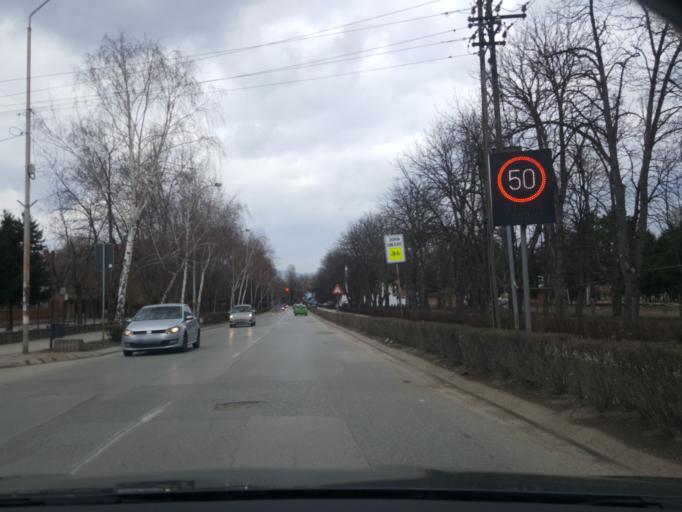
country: RS
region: Central Serbia
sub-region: Nisavski Okrug
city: Nis
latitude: 43.3134
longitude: 21.8795
